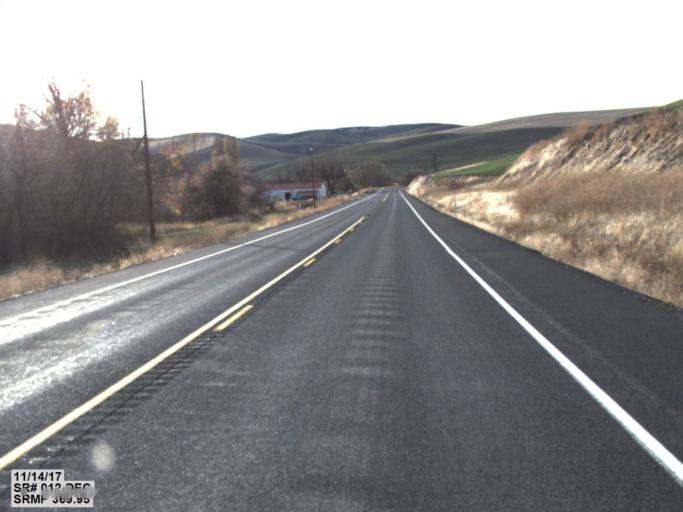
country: US
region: Washington
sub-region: Columbia County
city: Dayton
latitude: 46.3508
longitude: -117.9662
